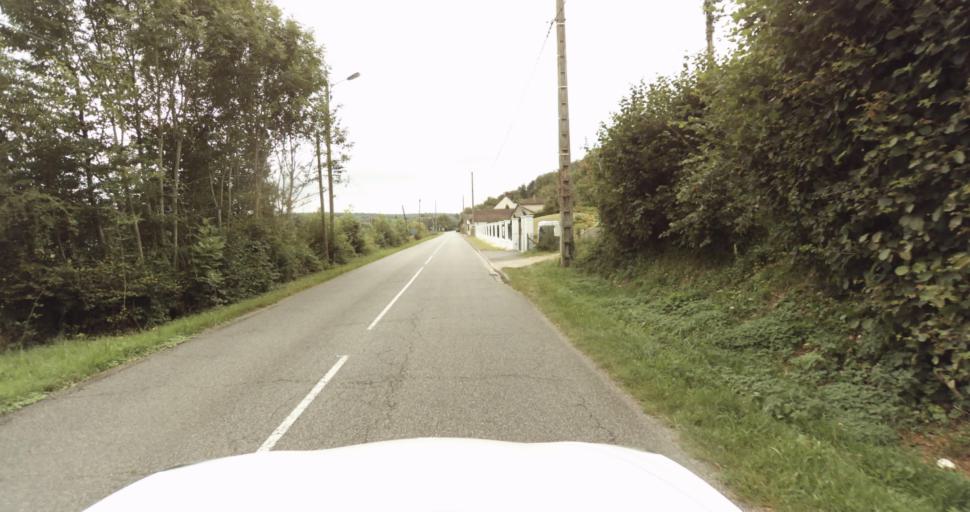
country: FR
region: Haute-Normandie
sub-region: Departement de l'Eure
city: Arnieres-sur-Iton
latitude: 49.0038
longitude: 1.1006
